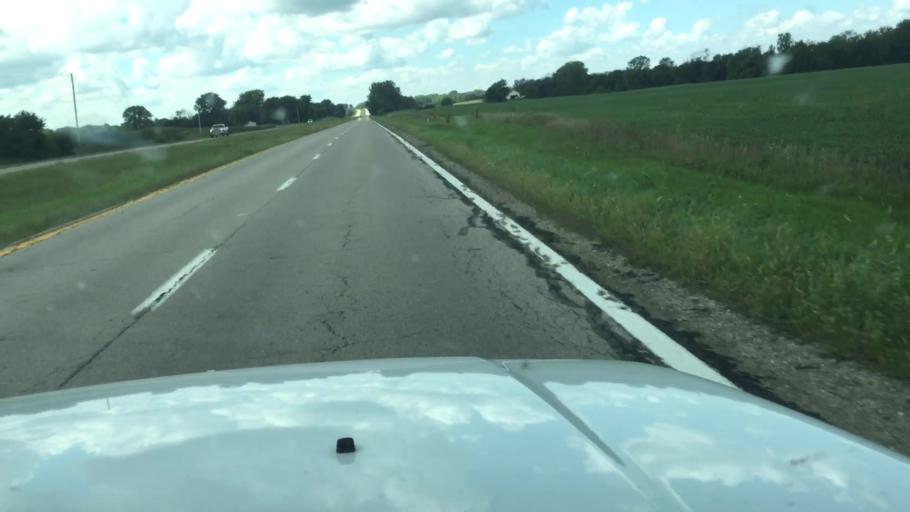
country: US
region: Ohio
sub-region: Madison County
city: Choctaw Lake
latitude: 39.9332
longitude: -83.5047
